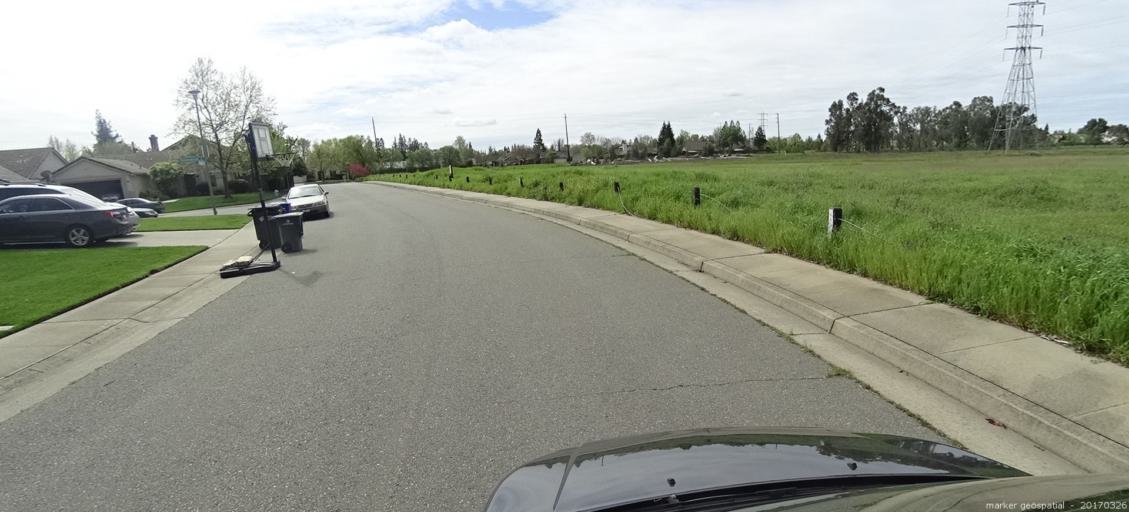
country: US
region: California
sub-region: Sacramento County
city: Laguna
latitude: 38.4394
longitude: -121.4314
